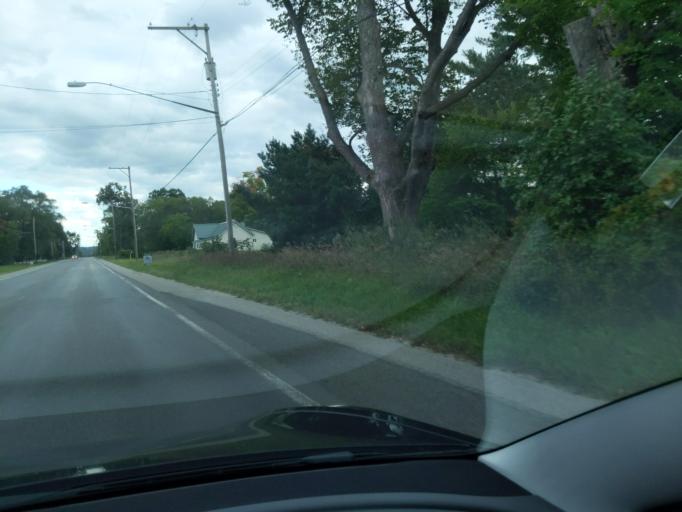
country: US
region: Michigan
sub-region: Kalkaska County
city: Rapid City
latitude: 44.8295
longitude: -85.2828
